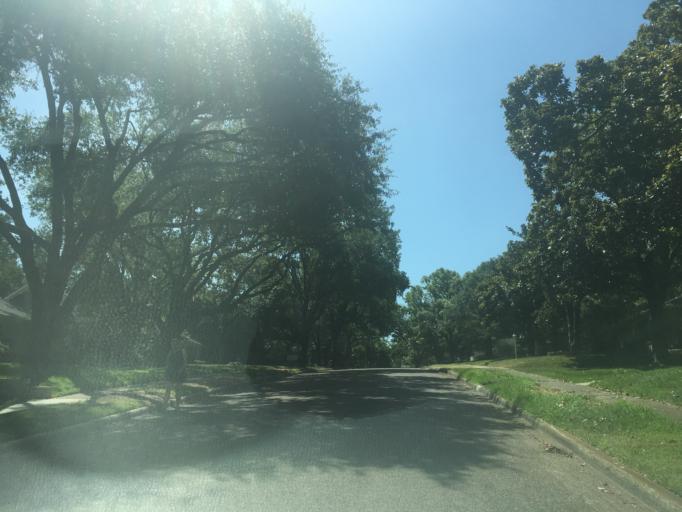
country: US
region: Texas
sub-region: Dallas County
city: Highland Park
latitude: 32.8699
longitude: -96.7256
